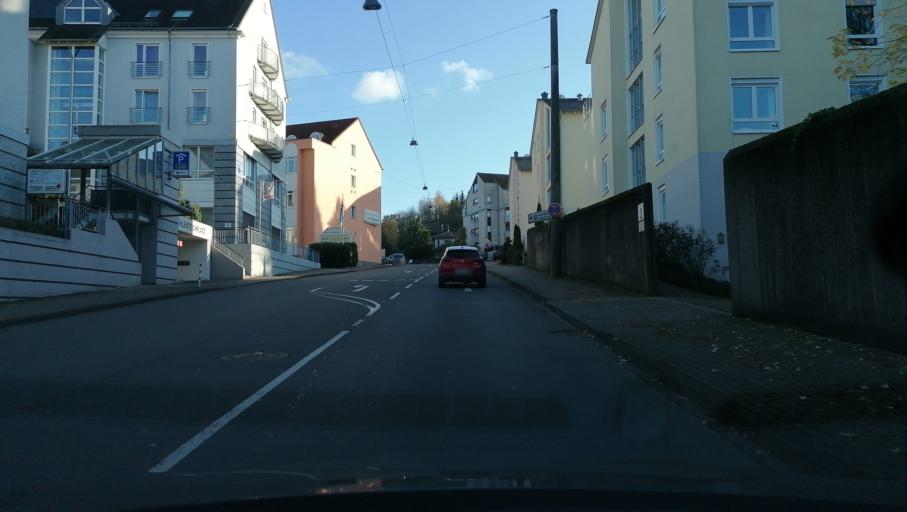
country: DE
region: North Rhine-Westphalia
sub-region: Regierungsbezirk Arnsberg
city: Schwelm
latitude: 51.2831
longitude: 7.2908
